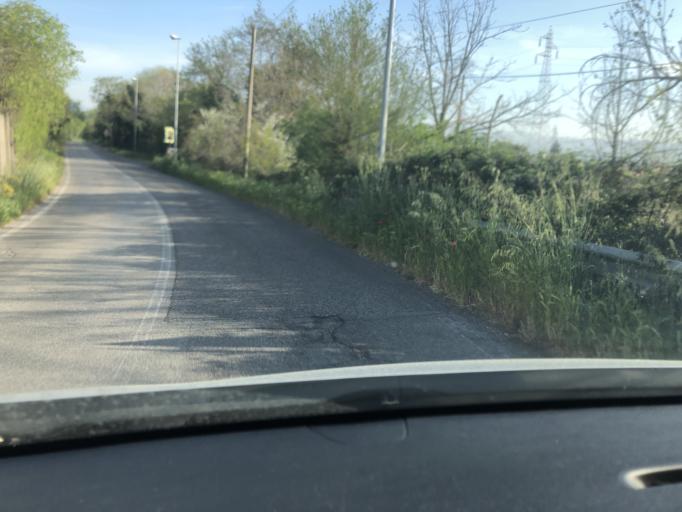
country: IT
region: Veneto
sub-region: Provincia di Verona
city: Verona
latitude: 45.4206
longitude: 11.0139
